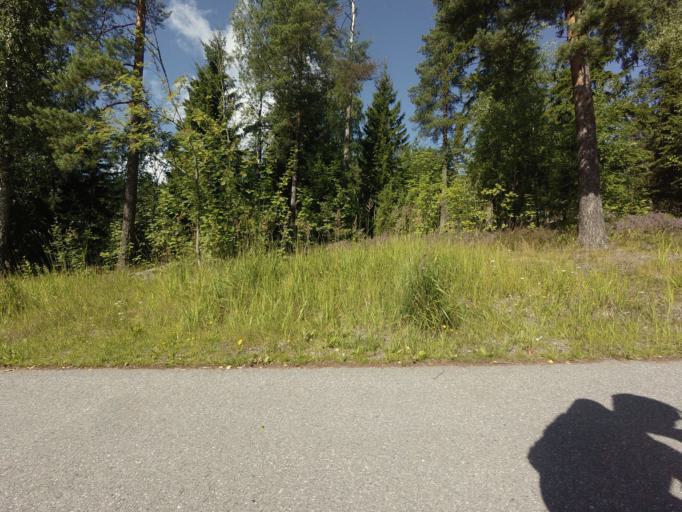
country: FI
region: Uusimaa
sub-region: Helsinki
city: Espoo
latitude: 60.1563
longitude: 24.6767
